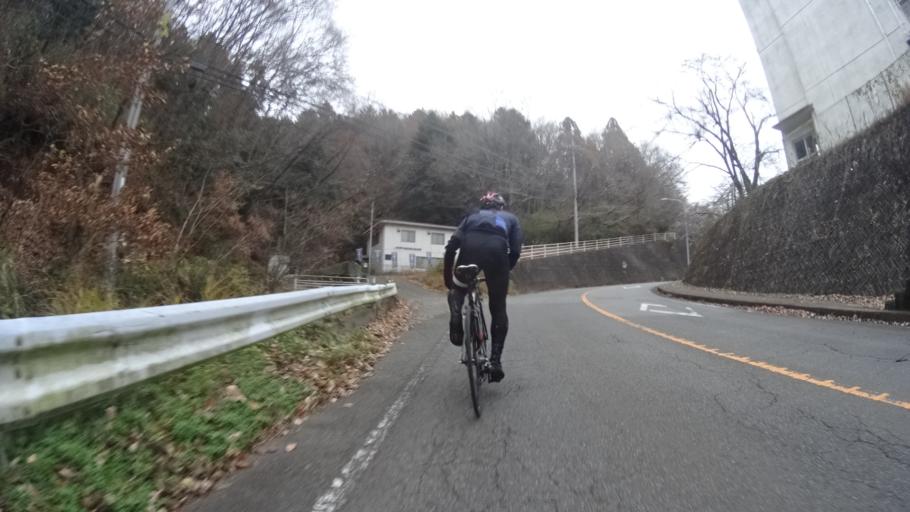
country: JP
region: Yamanashi
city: Uenohara
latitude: 35.6382
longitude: 139.1127
